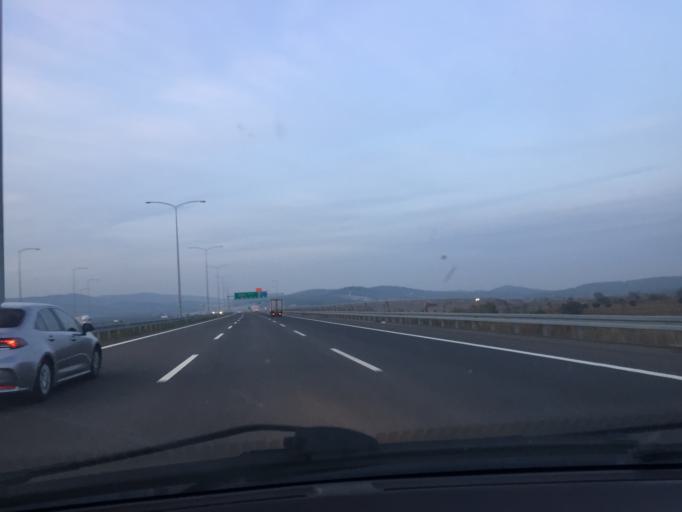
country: TR
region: Manisa
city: Halitpasa
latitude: 38.7617
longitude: 27.6603
